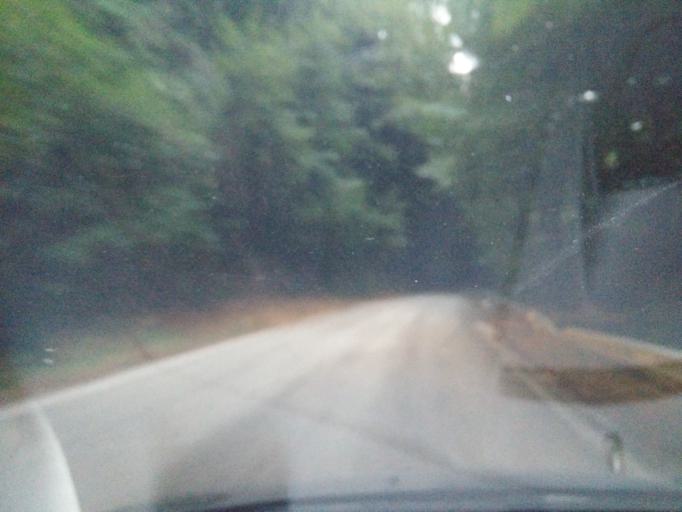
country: IT
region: Apulia
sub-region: Provincia di Foggia
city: Vico del Gargano
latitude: 41.8319
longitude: 16.0389
